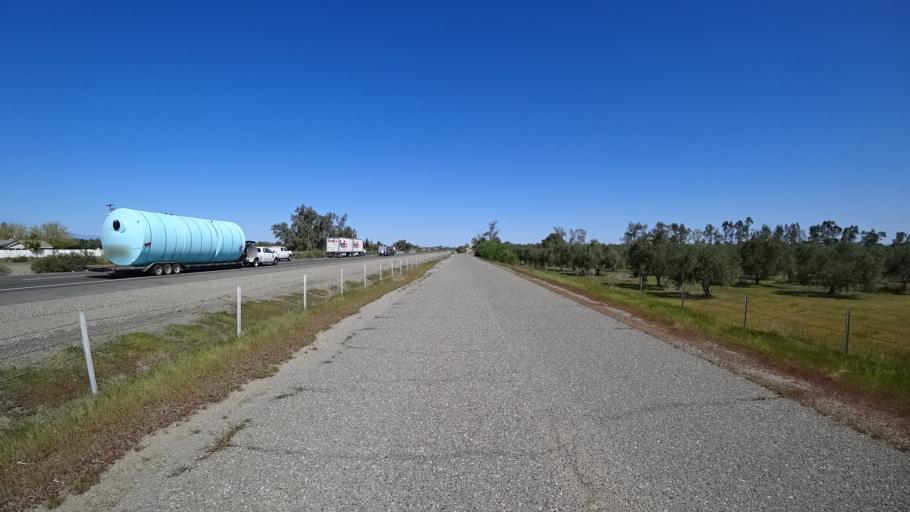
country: US
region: California
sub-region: Glenn County
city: Orland
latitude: 39.7026
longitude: -122.2053
